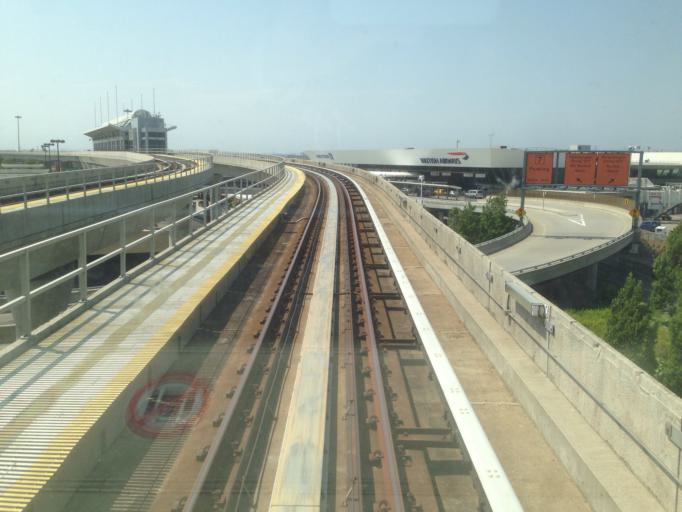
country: US
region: New York
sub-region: Nassau County
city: Inwood
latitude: 40.6478
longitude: -73.7809
